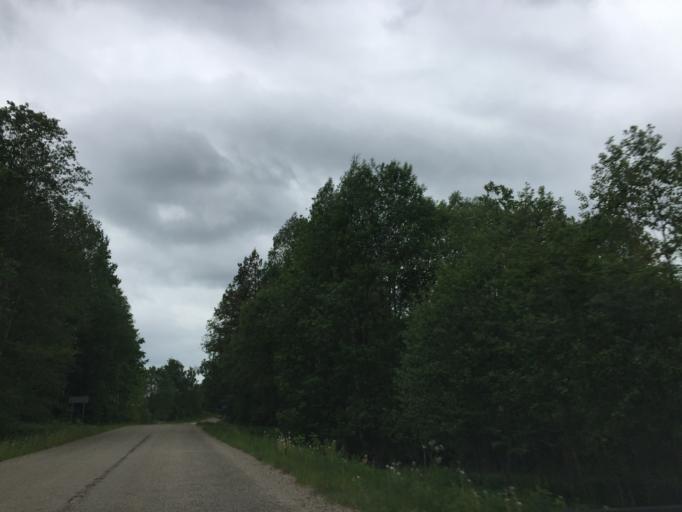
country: LV
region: Aglona
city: Aglona
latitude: 56.0791
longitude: 26.9137
